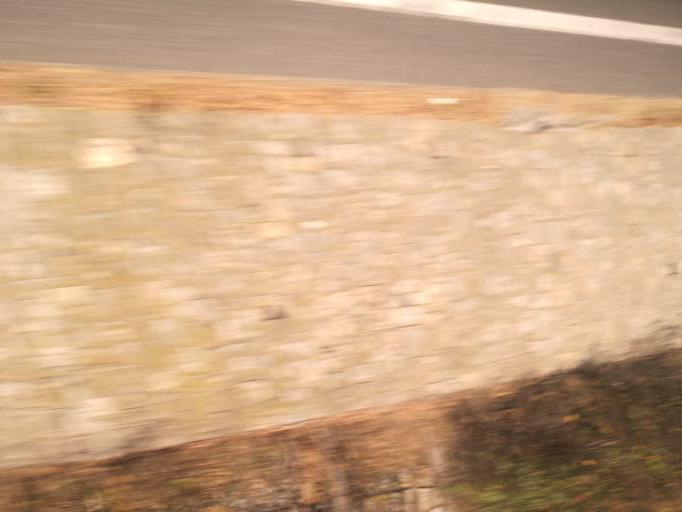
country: RO
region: Prahova
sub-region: Oras Breaza
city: Breaza de Sus
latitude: 45.2025
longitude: 25.6643
